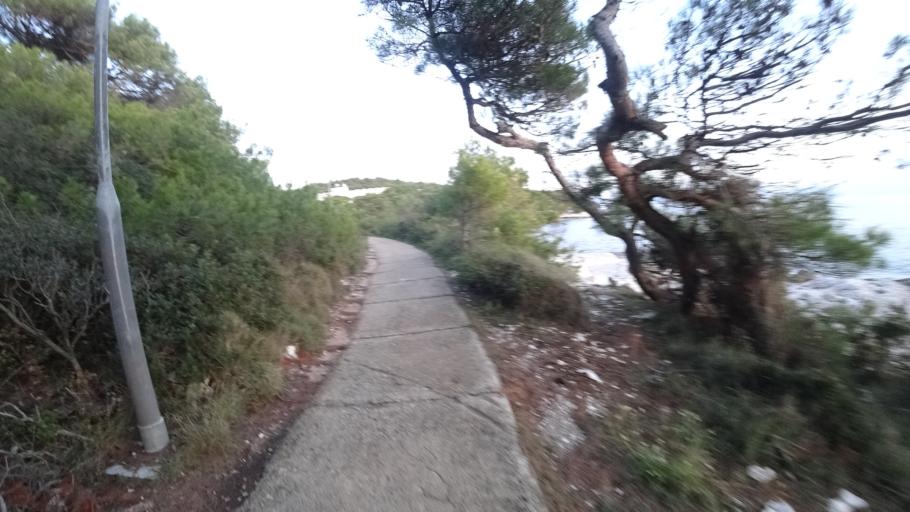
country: HR
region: Primorsko-Goranska
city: Mali Losinj
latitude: 44.5237
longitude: 14.4546
